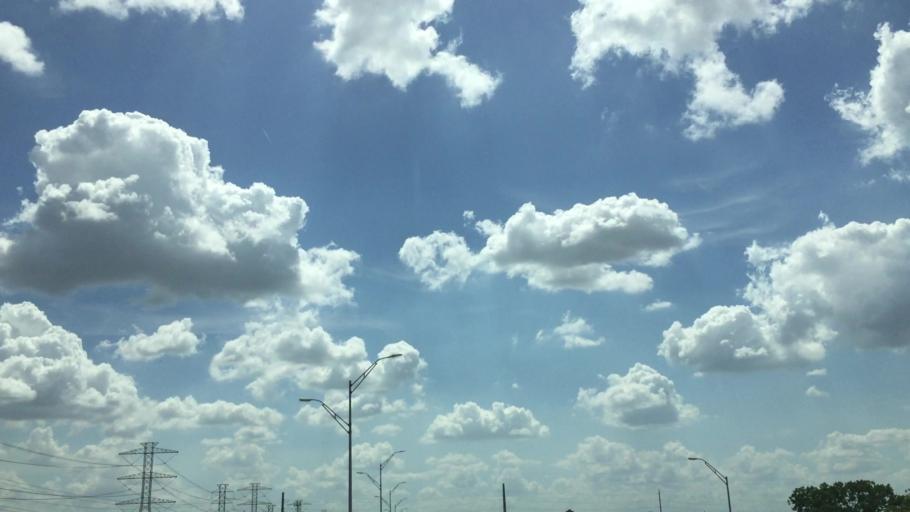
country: US
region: Texas
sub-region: Harris County
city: Piney Point Village
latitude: 29.7216
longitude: -95.5148
